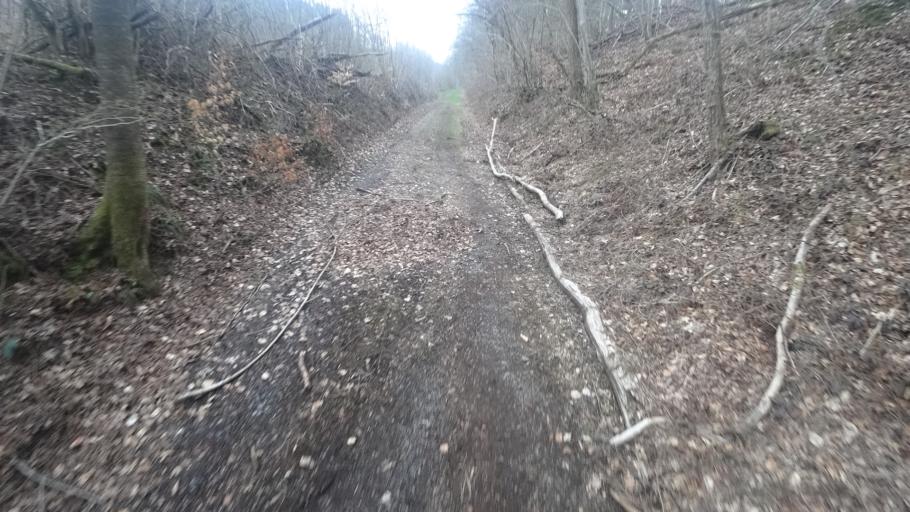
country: DE
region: Rheinland-Pfalz
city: Elben
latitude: 50.7480
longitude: 7.8319
